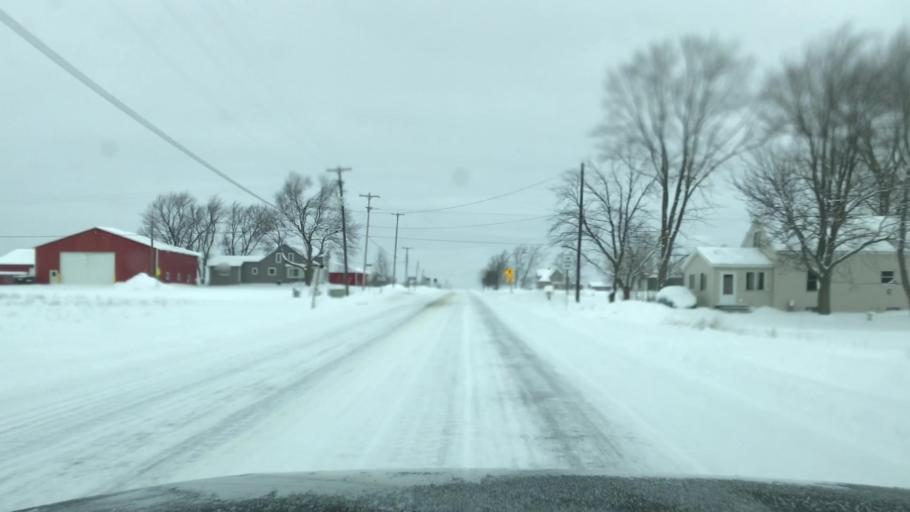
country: US
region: Michigan
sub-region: Ottawa County
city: Hudsonville
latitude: 42.8322
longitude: -85.8421
